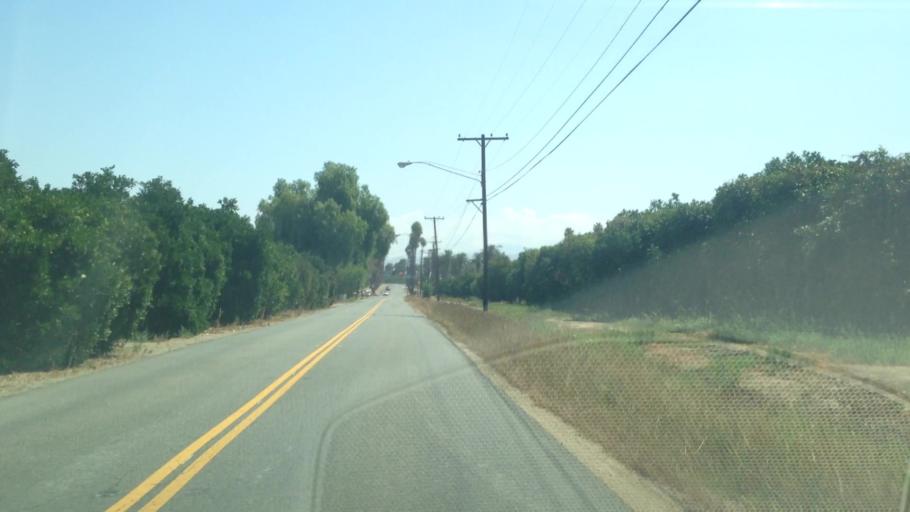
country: US
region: California
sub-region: Riverside County
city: Riverside
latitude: 33.8968
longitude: -117.4311
